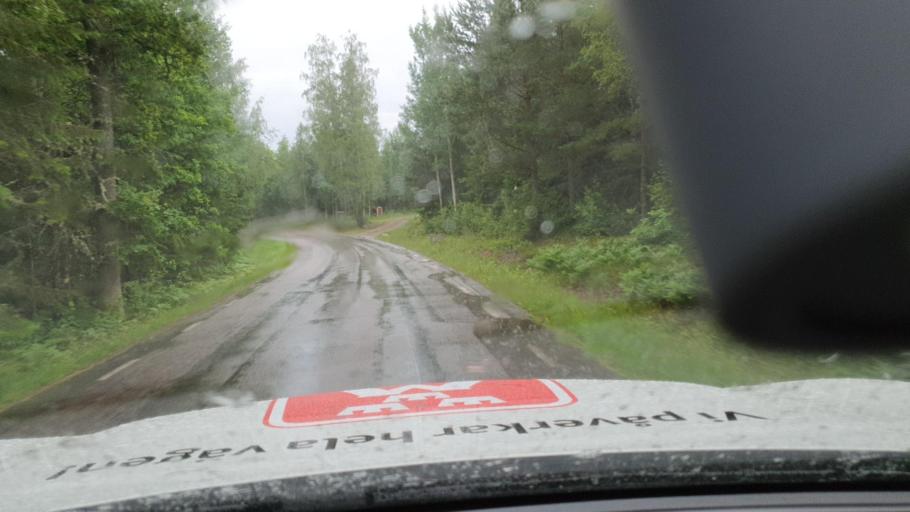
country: SE
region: Vaestra Goetaland
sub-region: Mariestads Kommun
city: Mariestad
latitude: 58.7720
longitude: 13.9388
